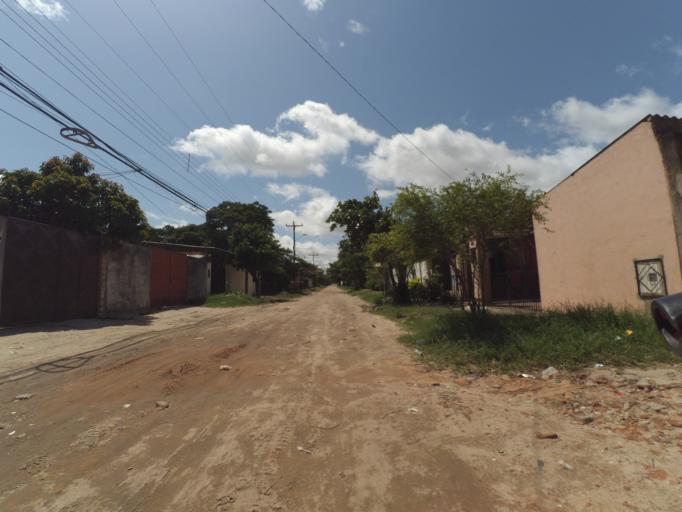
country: BO
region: Santa Cruz
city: Santa Cruz de la Sierra
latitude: -17.8044
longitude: -63.2181
